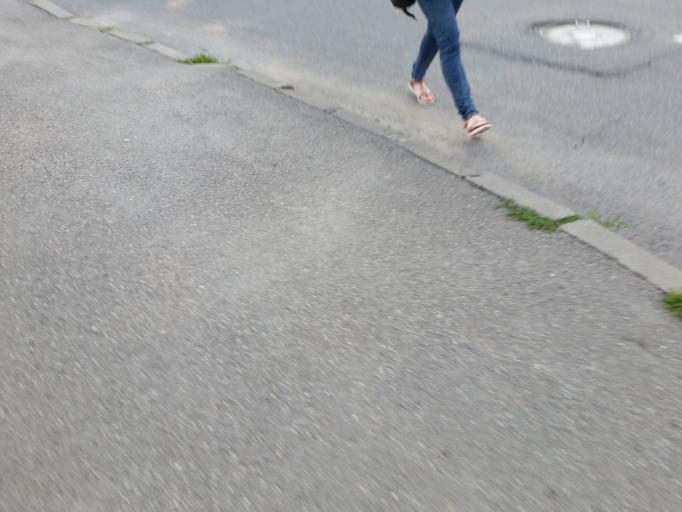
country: RO
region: Cluj
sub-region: Municipiul Cluj-Napoca
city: Cluj-Napoca
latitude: 46.7714
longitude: 23.5775
